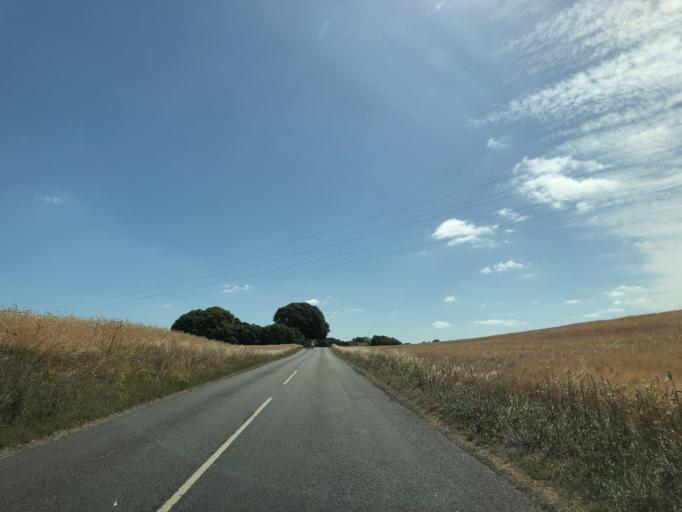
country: DK
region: North Denmark
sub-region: Vesthimmerland Kommune
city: Alestrup
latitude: 56.5757
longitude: 9.5360
